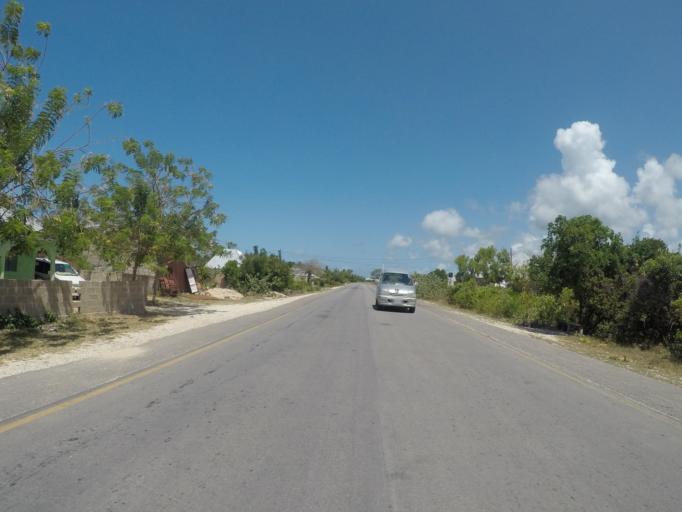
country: TZ
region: Zanzibar Central/South
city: Nganane
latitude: -6.3088
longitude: 39.5406
